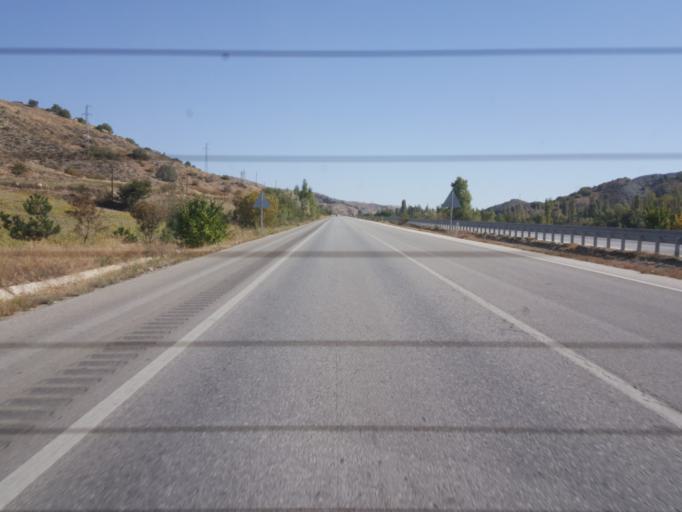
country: TR
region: Corum
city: Sungurlu
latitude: 40.1934
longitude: 34.5054
